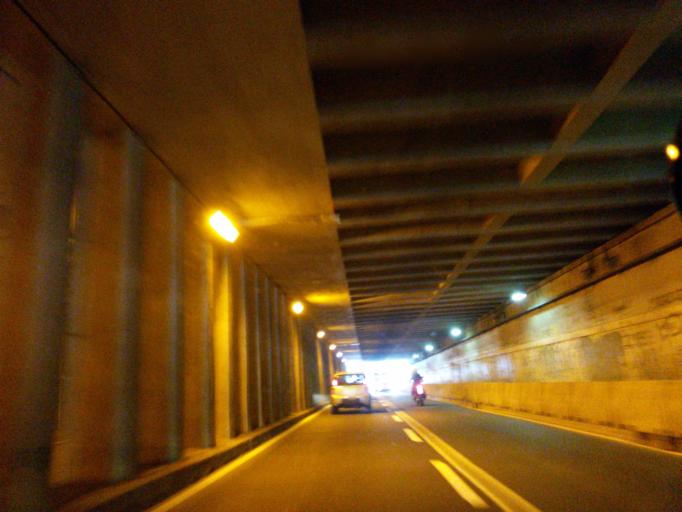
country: IT
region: Liguria
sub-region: Provincia di Genova
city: Genoa
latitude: 44.4067
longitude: 8.9487
